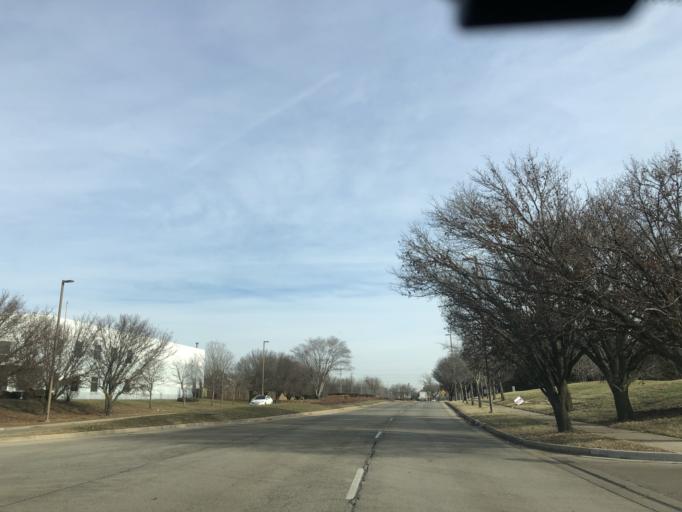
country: US
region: Illinois
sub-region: Cook County
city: Lemont
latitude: 41.6962
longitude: -88.0097
